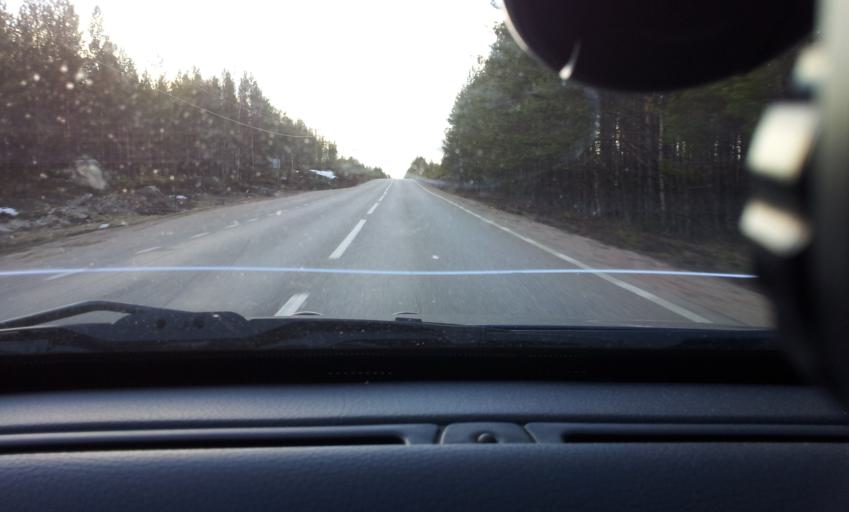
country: SE
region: Vaesternorrland
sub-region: Ange Kommun
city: Ange
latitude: 62.0926
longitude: 15.0885
